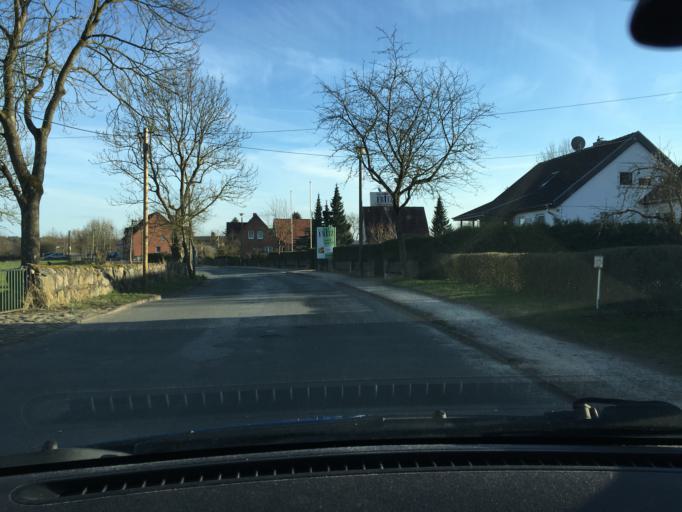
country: DE
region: Mecklenburg-Vorpommern
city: Feldstadt
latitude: 53.5956
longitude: 11.4043
